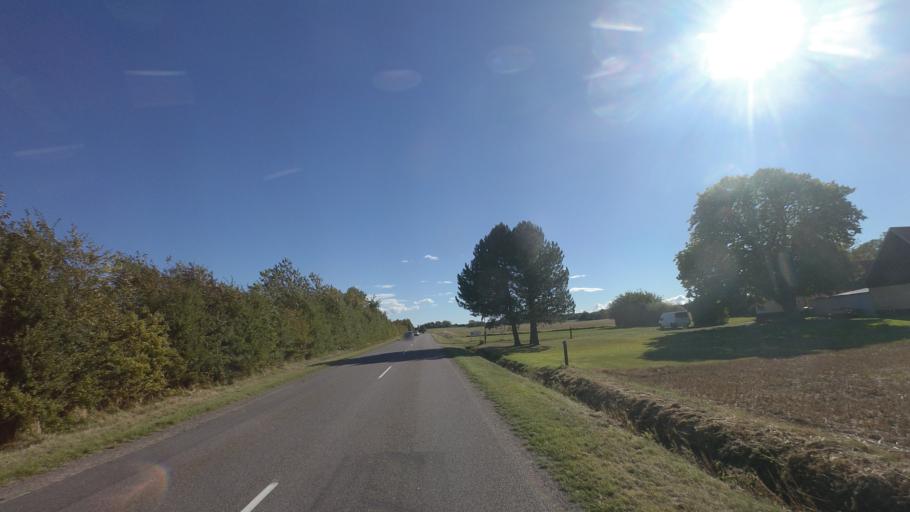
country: DK
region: Capital Region
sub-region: Bornholm Kommune
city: Nexo
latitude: 55.1117
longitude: 15.1101
